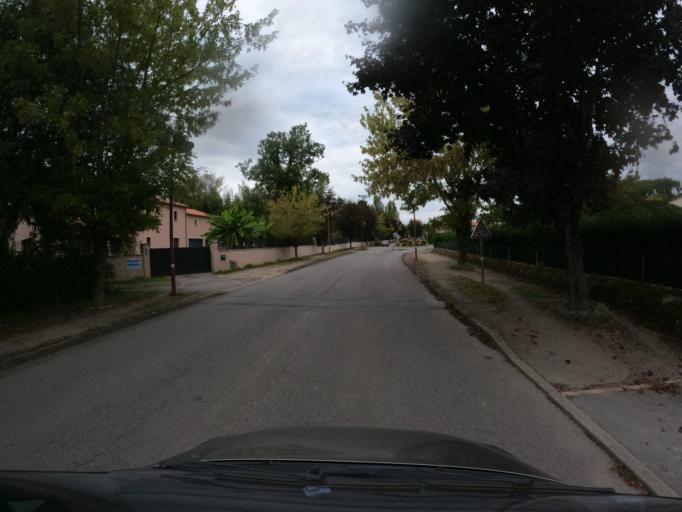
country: FR
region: Poitou-Charentes
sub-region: Departement des Deux-Sevres
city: Parthenay
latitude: 46.6551
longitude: -0.2486
